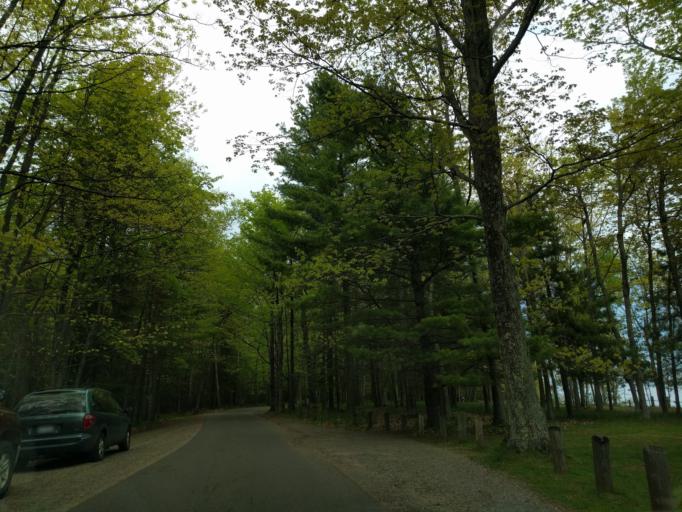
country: US
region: Michigan
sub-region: Marquette County
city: Marquette
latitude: 46.5819
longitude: -87.3805
